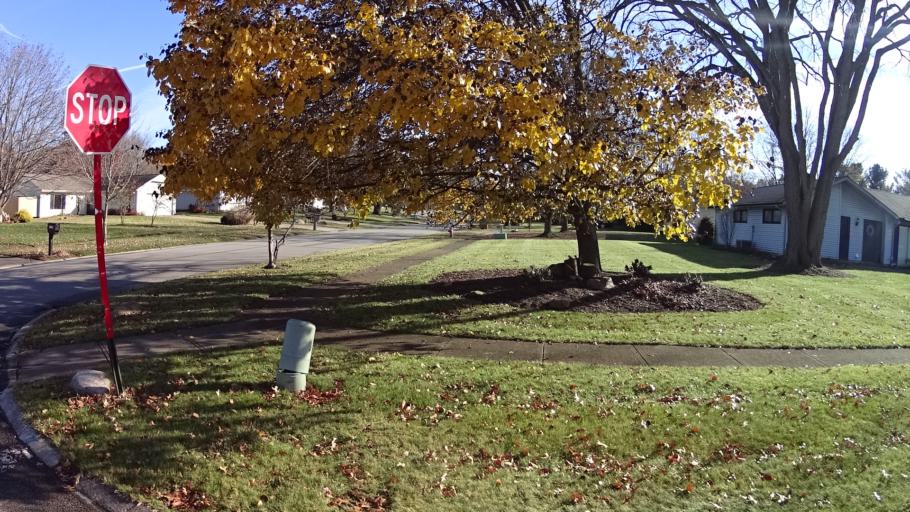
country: US
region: Ohio
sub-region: Lorain County
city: North Ridgeville
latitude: 41.3981
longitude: -81.9729
